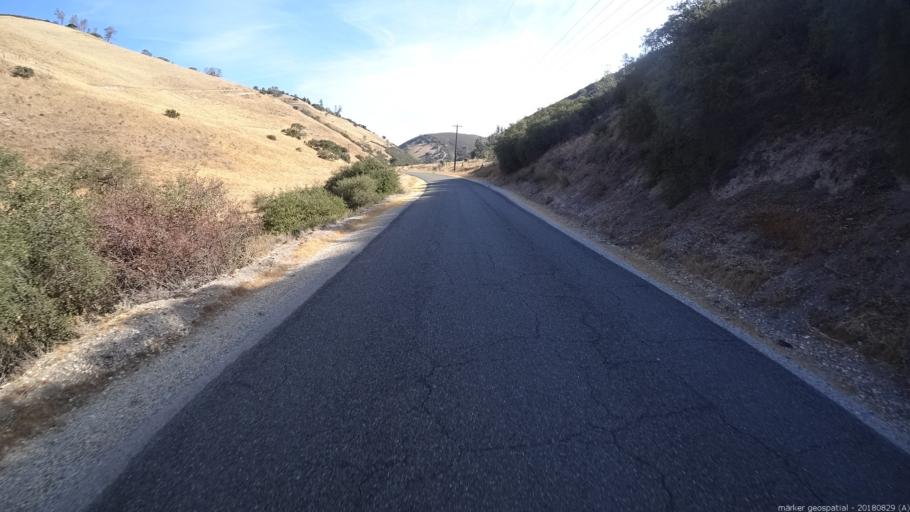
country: US
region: California
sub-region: Monterey County
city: King City
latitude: 35.9938
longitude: -121.0725
